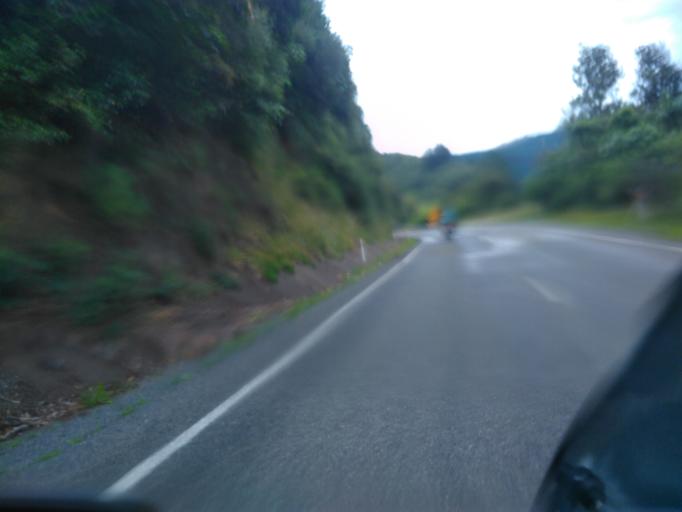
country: NZ
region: Bay of Plenty
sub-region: Opotiki District
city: Opotiki
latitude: -38.2532
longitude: 177.3013
